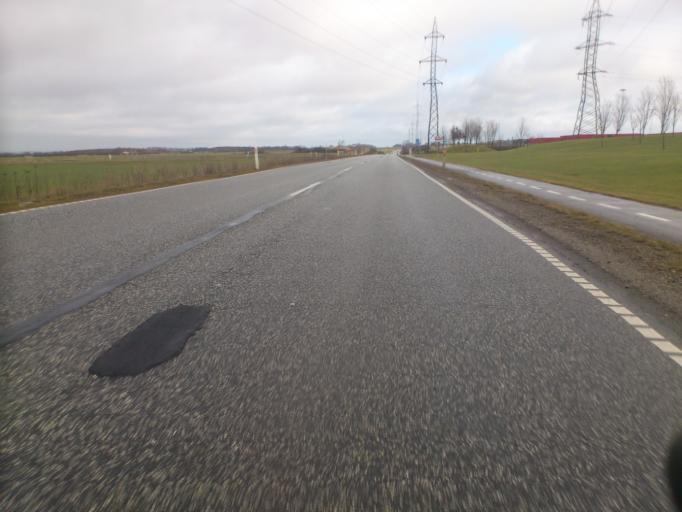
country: DK
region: South Denmark
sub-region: Fredericia Kommune
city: Fredericia
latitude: 55.5913
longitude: 9.7182
